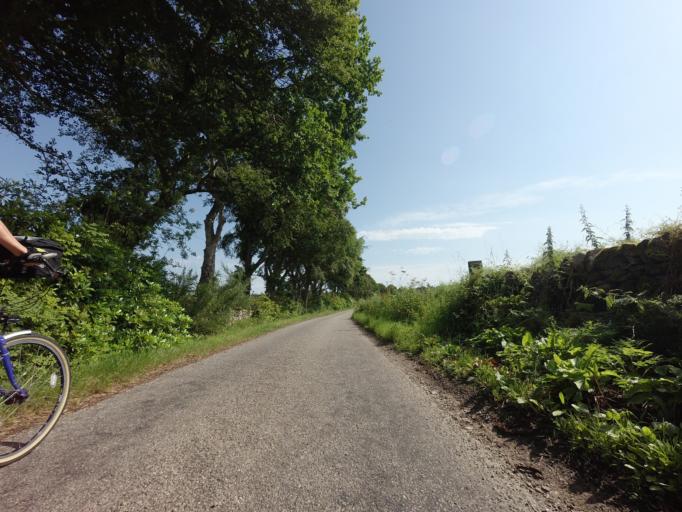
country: GB
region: Scotland
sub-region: Highland
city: Alness
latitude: 57.7133
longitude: -4.2213
